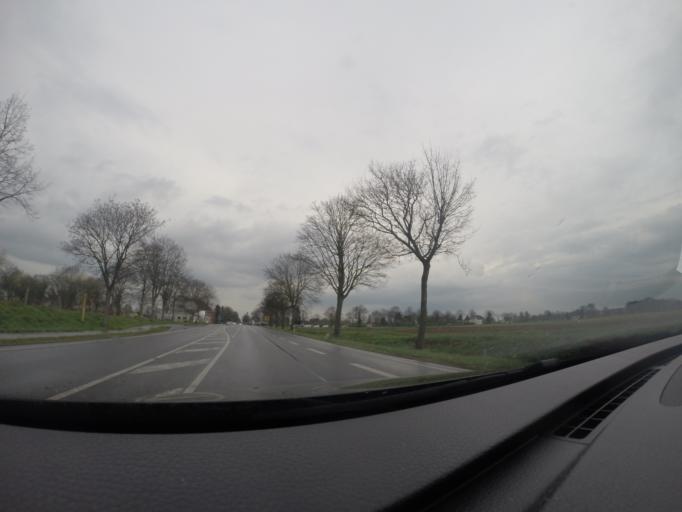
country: DE
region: North Rhine-Westphalia
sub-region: Regierungsbezirk Dusseldorf
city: Alpen
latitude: 51.5928
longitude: 6.5379
